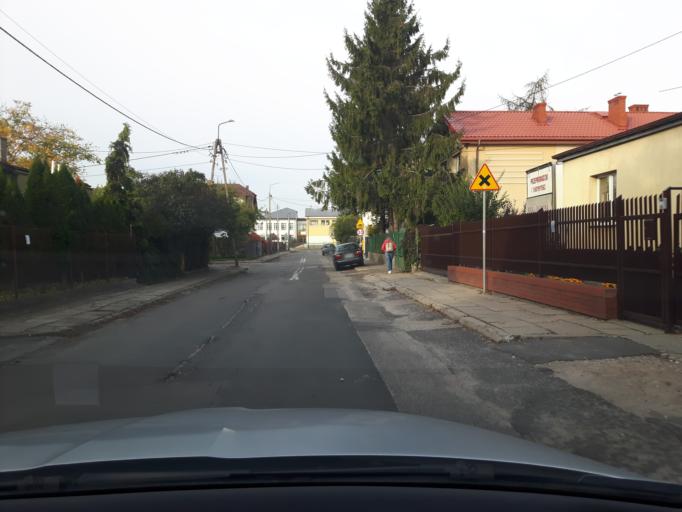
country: PL
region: Masovian Voivodeship
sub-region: Powiat wolominski
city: Zabki
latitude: 52.2867
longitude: 21.1148
